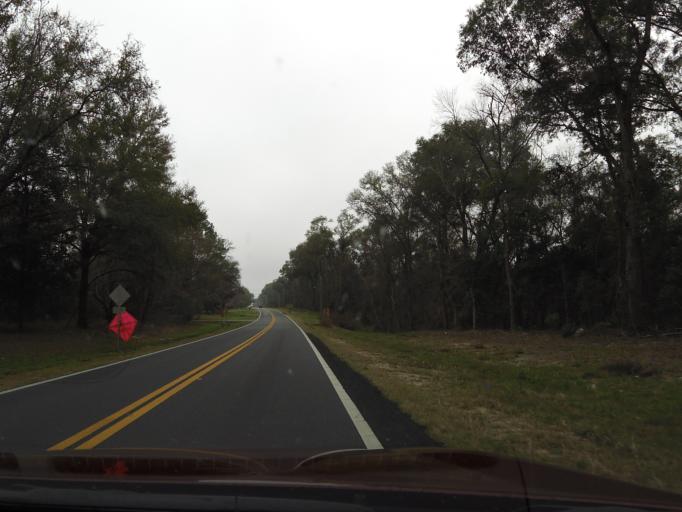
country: US
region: Florida
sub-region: Alachua County
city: High Springs
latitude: 29.8465
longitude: -82.5855
